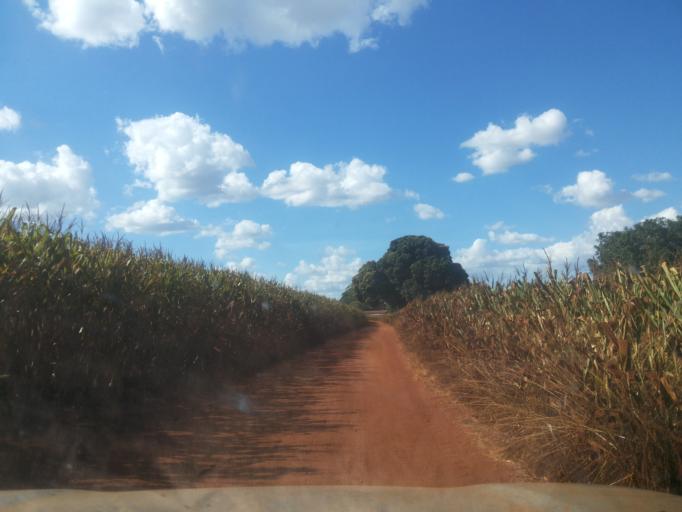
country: BR
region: Minas Gerais
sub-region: Capinopolis
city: Capinopolis
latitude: -18.5823
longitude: -49.4947
